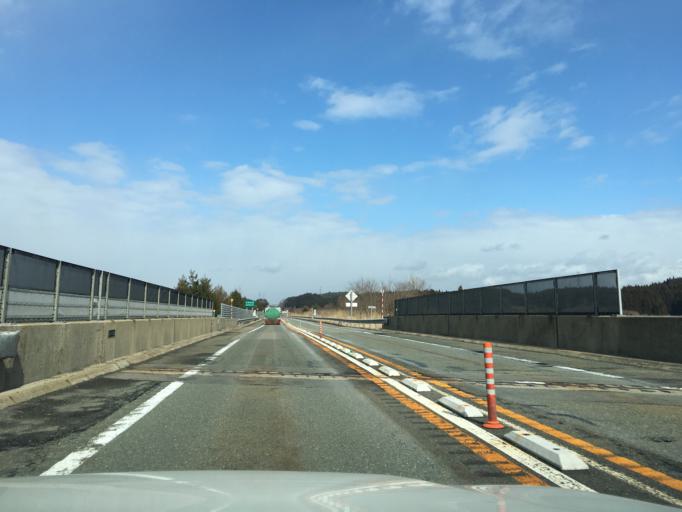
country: JP
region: Akita
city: Akita Shi
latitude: 39.7936
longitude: 140.1020
